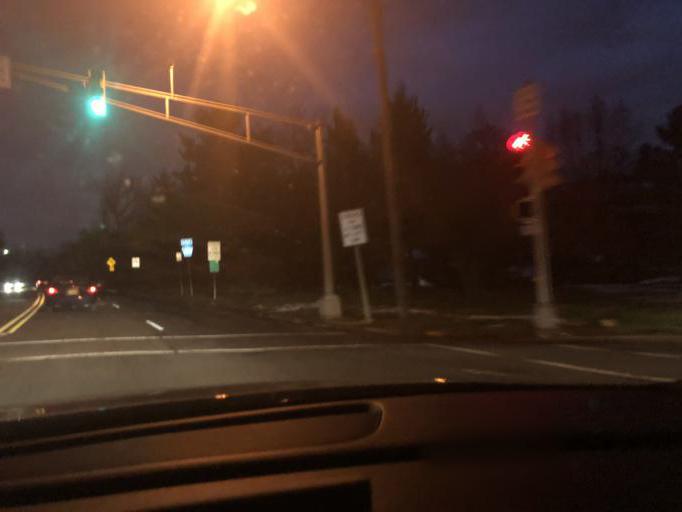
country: US
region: New Jersey
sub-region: Essex County
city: Short Hills
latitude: 40.7540
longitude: -74.3067
